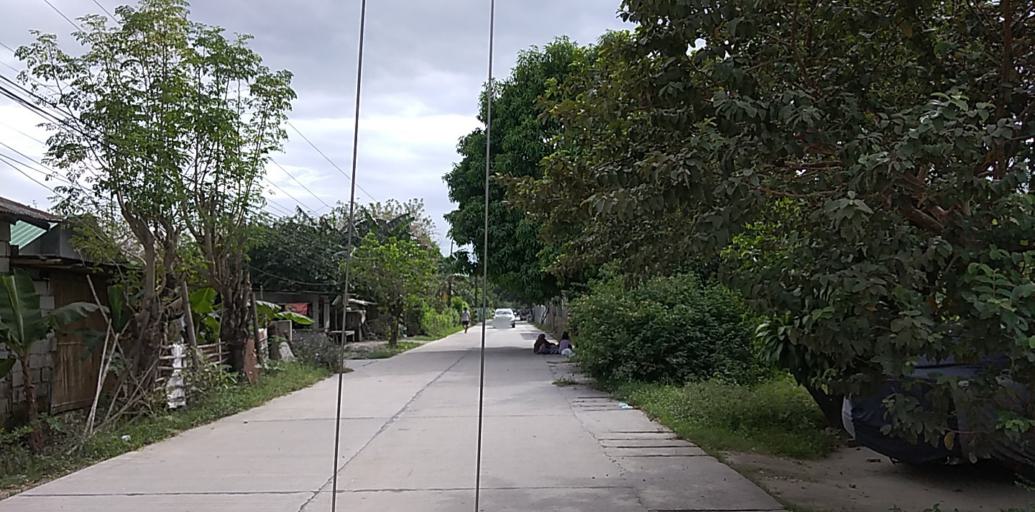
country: PH
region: Central Luzon
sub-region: Province of Pampanga
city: Pulung Santol
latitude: 15.0468
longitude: 120.5558
